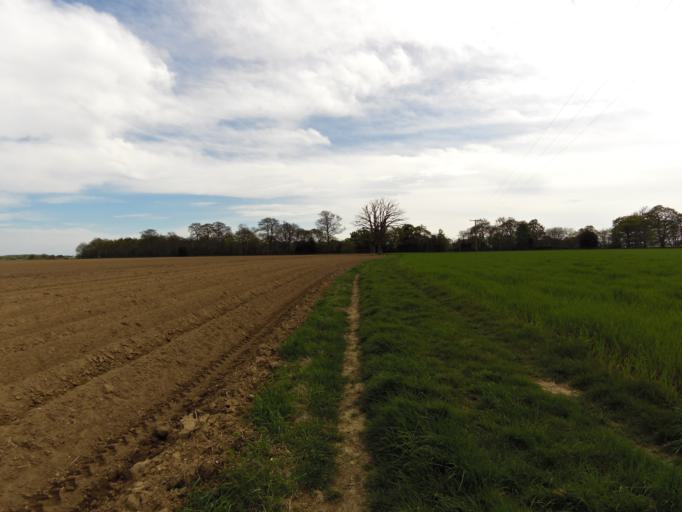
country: GB
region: England
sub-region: Suffolk
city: Ipswich
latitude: 51.9992
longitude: 1.1426
